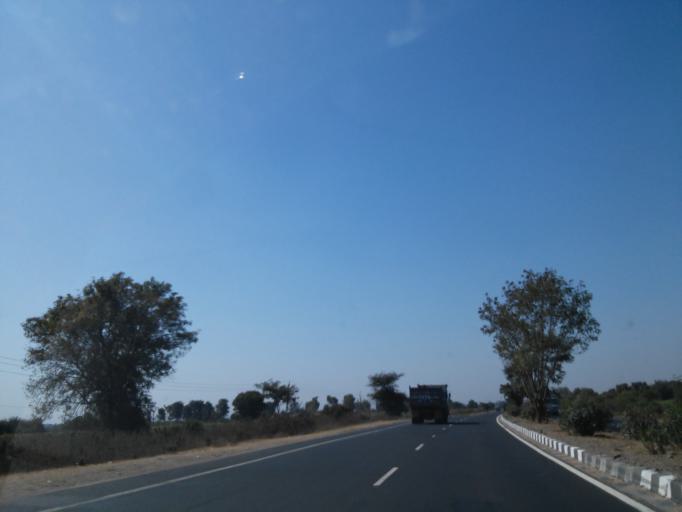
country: IN
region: Gujarat
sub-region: Sabar Kantha
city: Modasa
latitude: 23.6054
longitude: 73.2257
